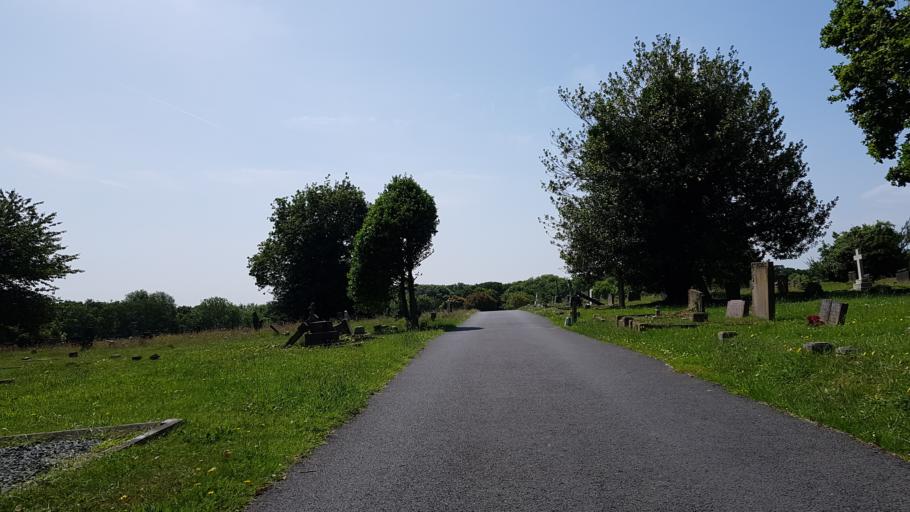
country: GB
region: England
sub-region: Isle of Wight
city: Cowes
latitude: 50.7495
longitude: -1.2999
